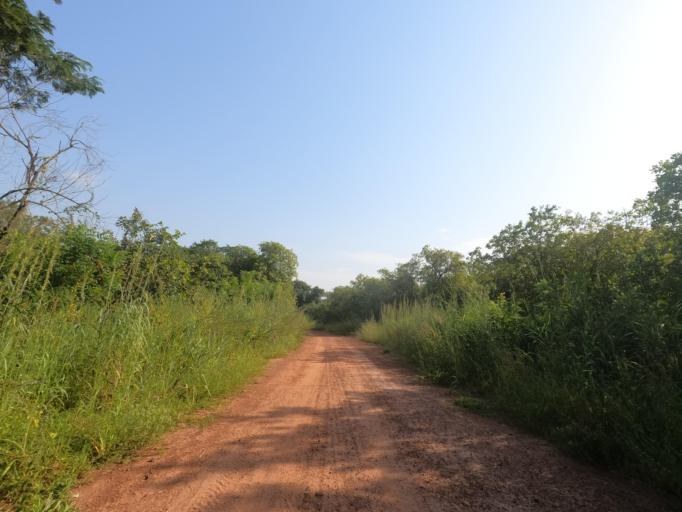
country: SN
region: Sedhiou
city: Sedhiou
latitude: 12.4424
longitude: -15.7386
